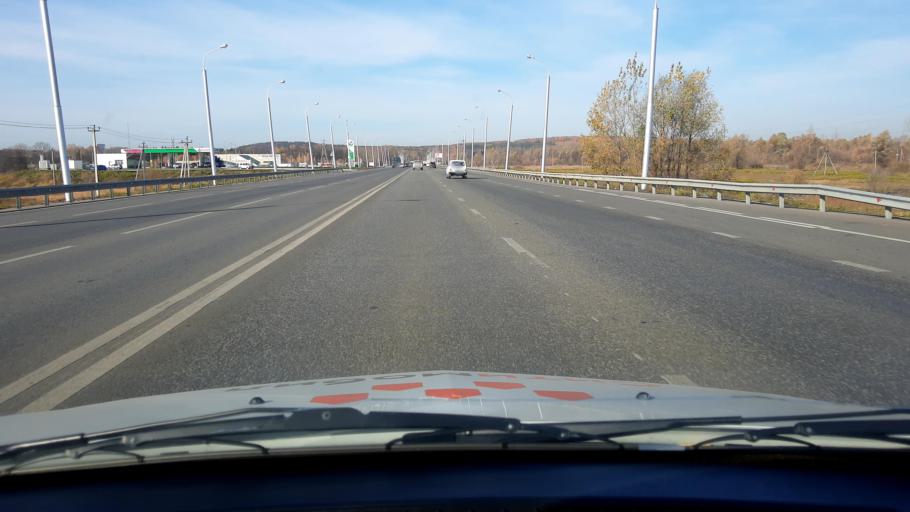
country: RU
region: Bashkortostan
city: Ufa
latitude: 54.8051
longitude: 56.1816
